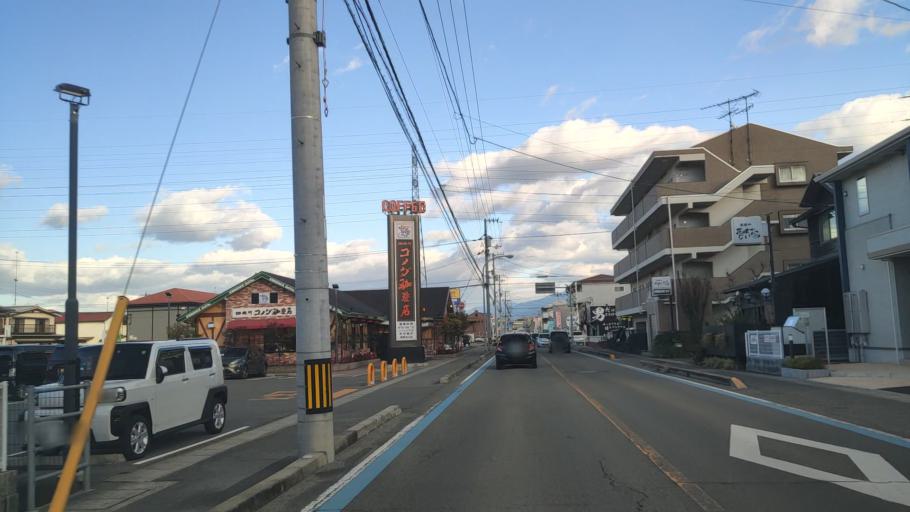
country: JP
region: Ehime
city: Saijo
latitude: 33.9152
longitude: 133.1677
